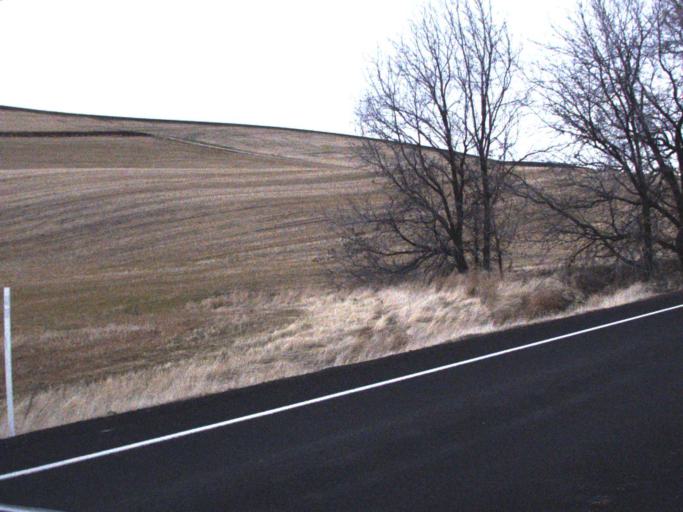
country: US
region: Washington
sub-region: Walla Walla County
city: Waitsburg
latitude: 46.2270
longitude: -118.1376
